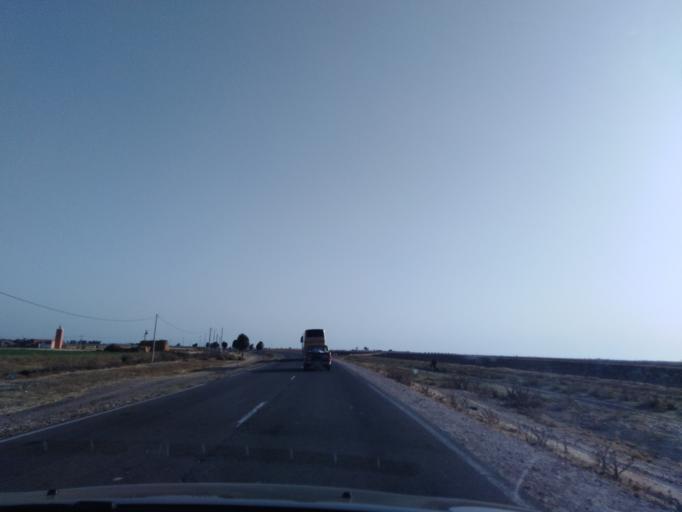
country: MA
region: Doukkala-Abda
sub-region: Safi
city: Youssoufia
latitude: 32.4894
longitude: -8.7644
